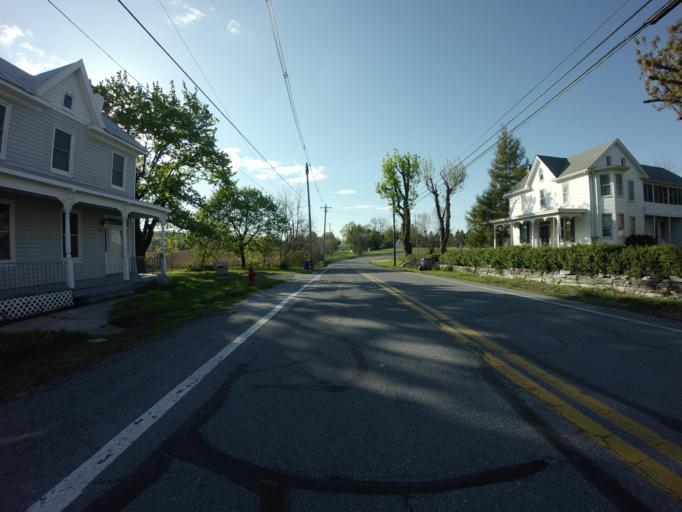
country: US
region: Maryland
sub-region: Frederick County
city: Woodsboro
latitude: 39.5396
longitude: -77.3173
